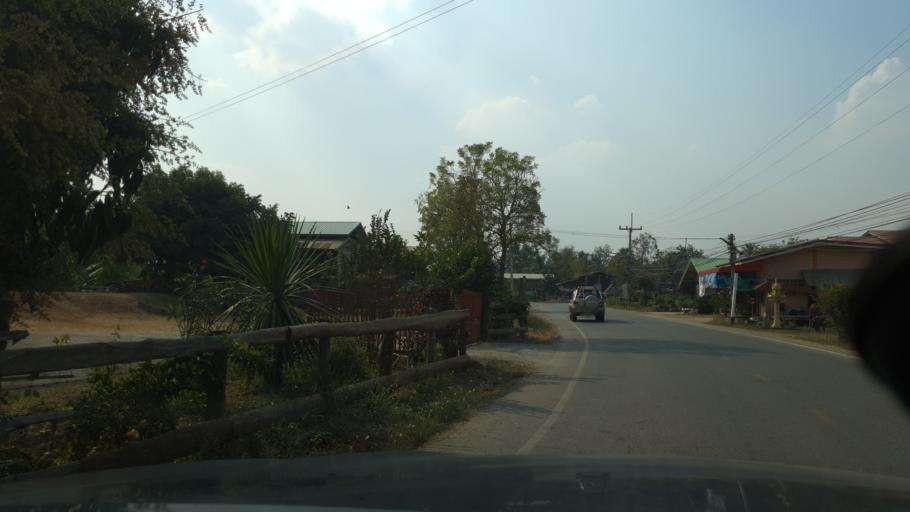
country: TH
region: Sukhothai
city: Ban Dan Lan Hoi
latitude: 17.1166
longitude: 99.5366
